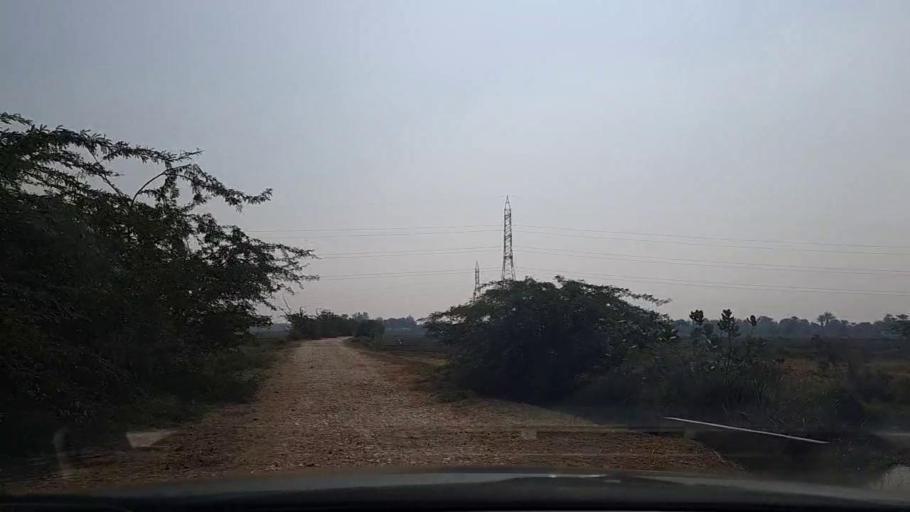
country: PK
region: Sindh
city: Mirpur Sakro
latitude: 24.5691
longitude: 67.7761
